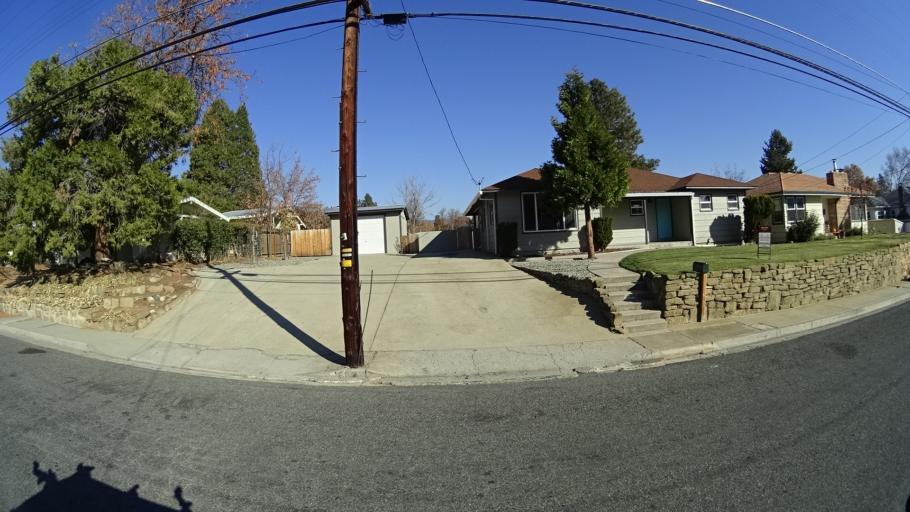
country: US
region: California
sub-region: Siskiyou County
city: Yreka
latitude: 41.7348
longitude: -122.6416
